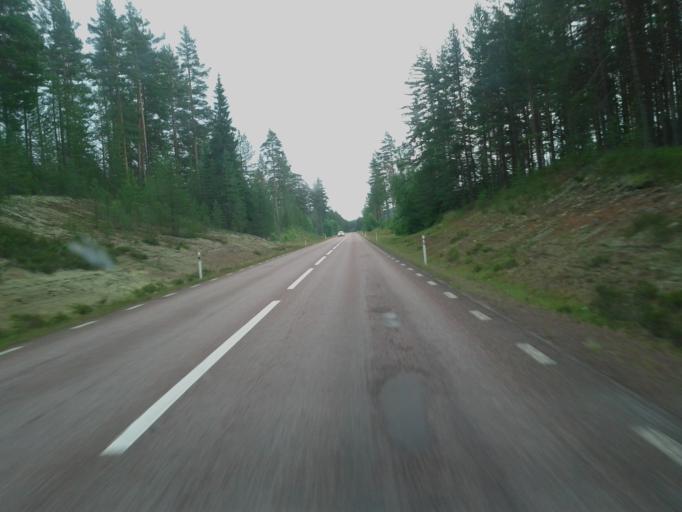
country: SE
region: Dalarna
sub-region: Mora Kommun
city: Mora
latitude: 61.1001
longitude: 14.2951
